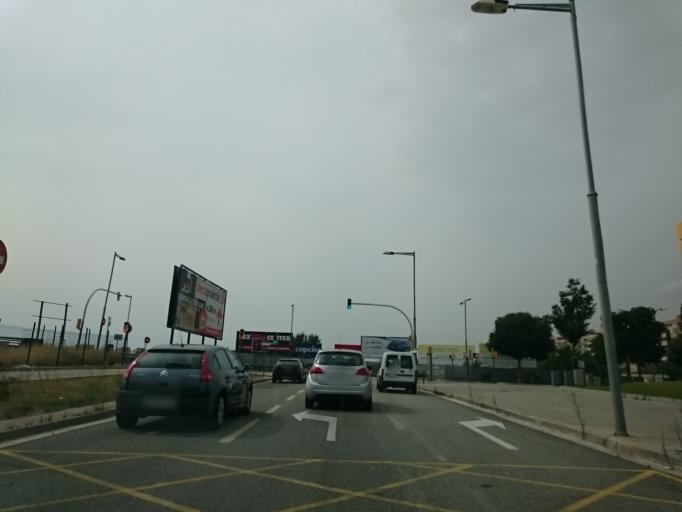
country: ES
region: Catalonia
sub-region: Provincia de Barcelona
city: Sant Andreu de Palomar
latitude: 41.4429
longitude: 2.1944
